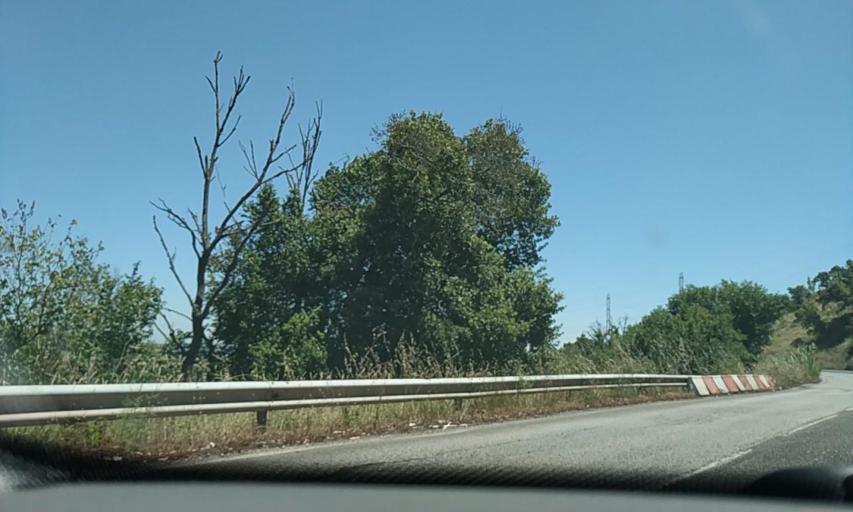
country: PT
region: Lisbon
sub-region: Odivelas
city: Canecas
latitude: 38.8571
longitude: -9.2098
